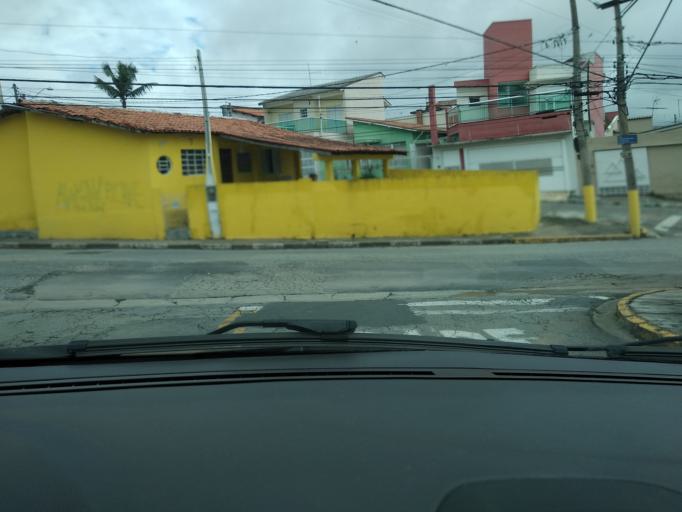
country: BR
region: Sao Paulo
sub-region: Mogi das Cruzes
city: Mogi das Cruzes
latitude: -23.5313
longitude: -46.1783
